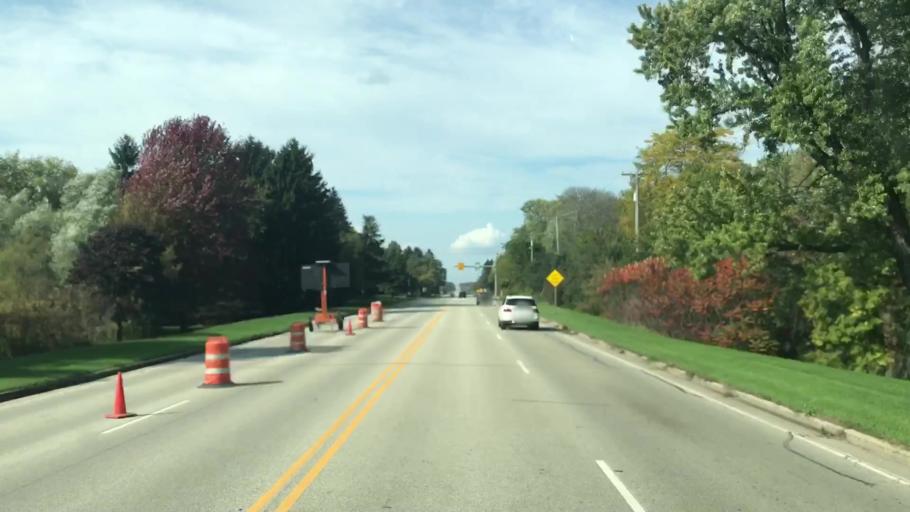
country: US
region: Wisconsin
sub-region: Ozaukee County
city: Mequon
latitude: 43.2216
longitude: -88.0152
